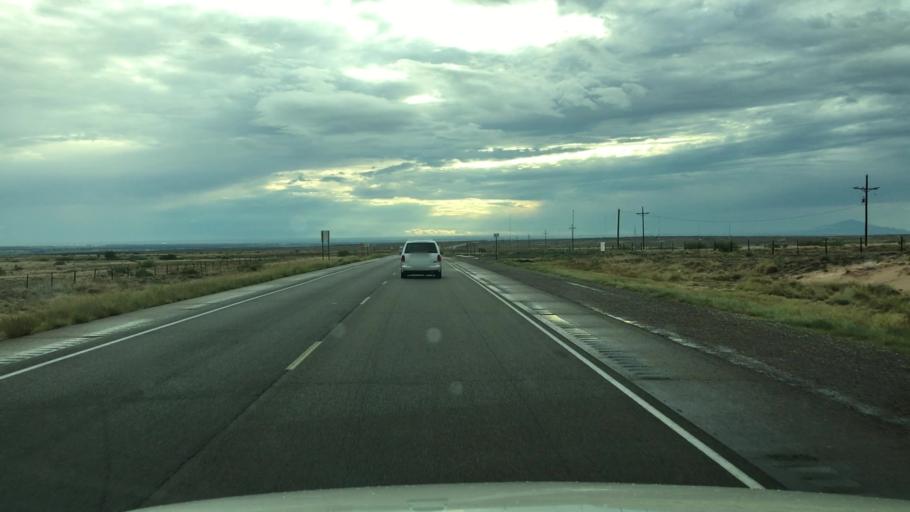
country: US
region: New Mexico
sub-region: Chaves County
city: Roswell
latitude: 33.4000
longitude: -104.3424
